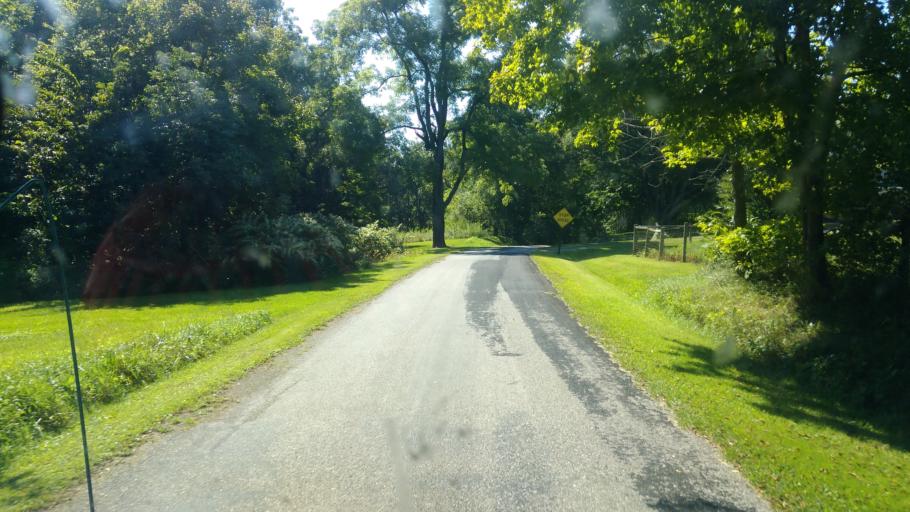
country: US
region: Ohio
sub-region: Ashland County
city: Ashland
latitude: 40.9468
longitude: -82.2787
